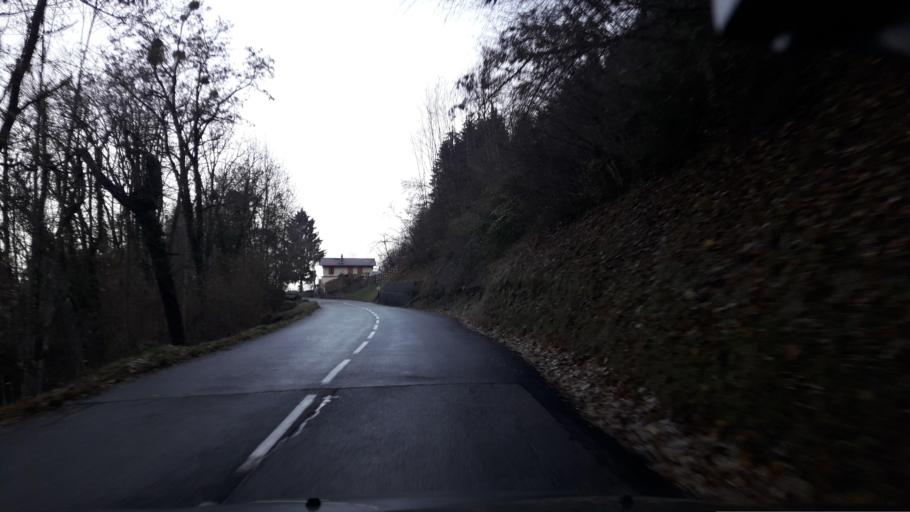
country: FR
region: Rhone-Alpes
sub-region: Departement de l'Isere
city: Allevard
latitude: 45.3960
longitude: 6.0840
